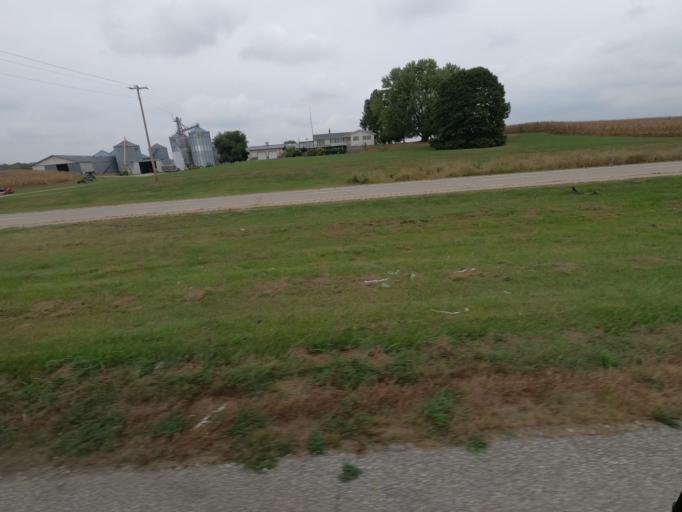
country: US
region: Iowa
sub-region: Wapello County
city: Eddyville
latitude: 41.1423
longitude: -92.6114
